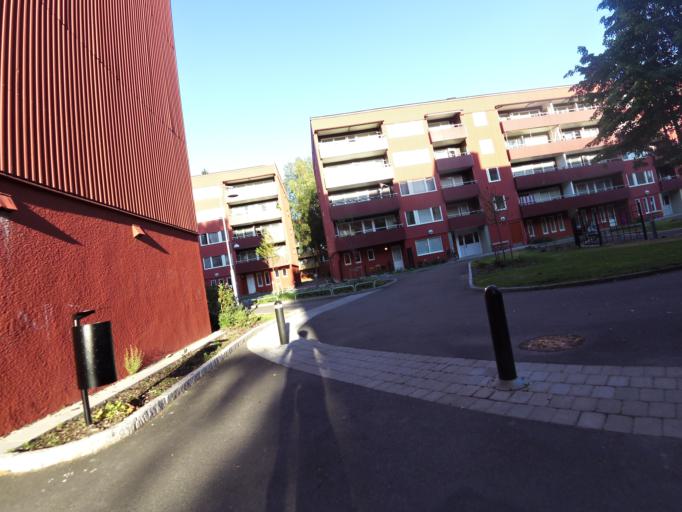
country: SE
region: Gaevleborg
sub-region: Gavle Kommun
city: Gavle
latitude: 60.6504
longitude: 17.1326
